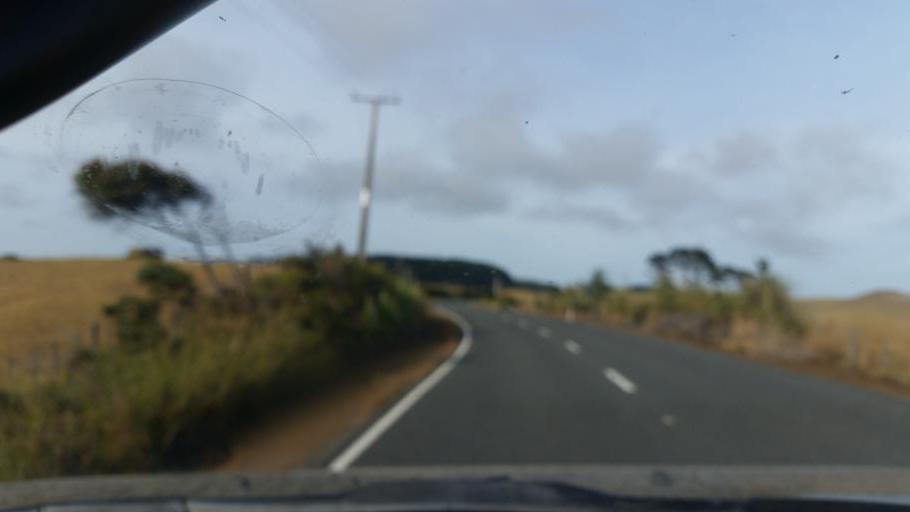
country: NZ
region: Northland
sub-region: Kaipara District
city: Dargaville
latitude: -36.2080
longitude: 174.0413
